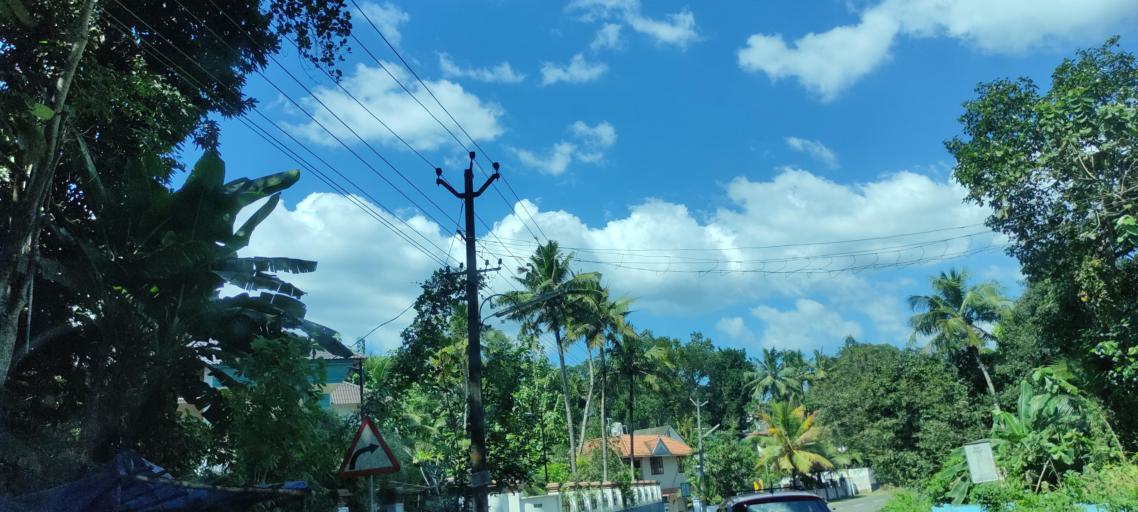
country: IN
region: Kerala
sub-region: Pattanamtitta
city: Adur
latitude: 9.1053
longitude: 76.6903
